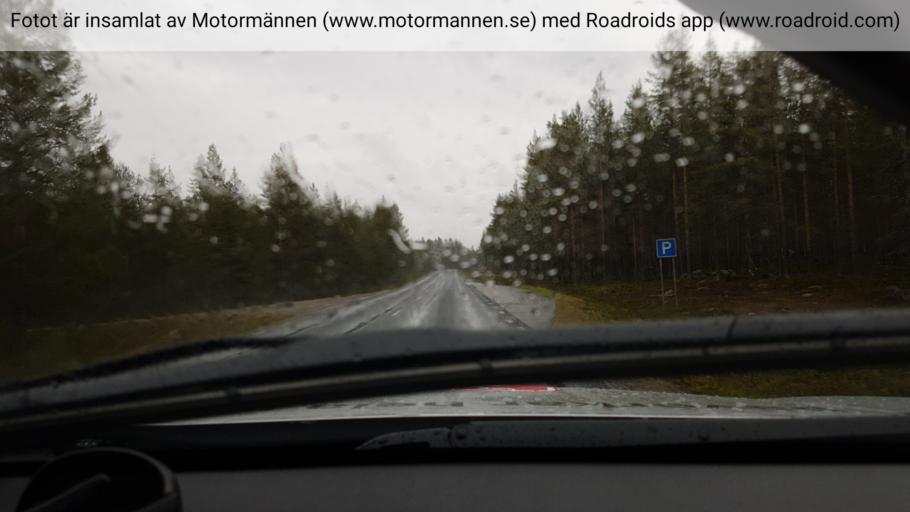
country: SE
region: Vaesterbotten
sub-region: Mala Kommun
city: Mala
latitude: 65.2145
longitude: 18.6695
